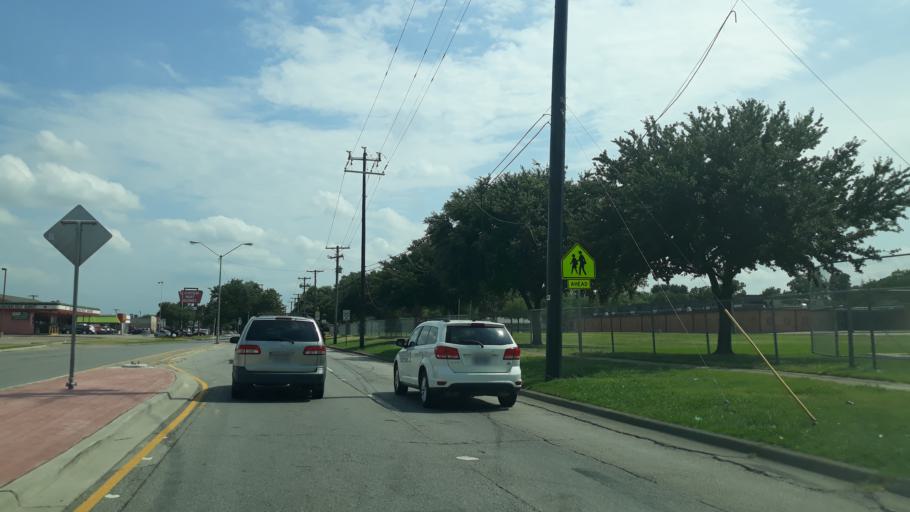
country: US
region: Texas
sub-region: Dallas County
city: Irving
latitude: 32.8360
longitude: -96.9765
